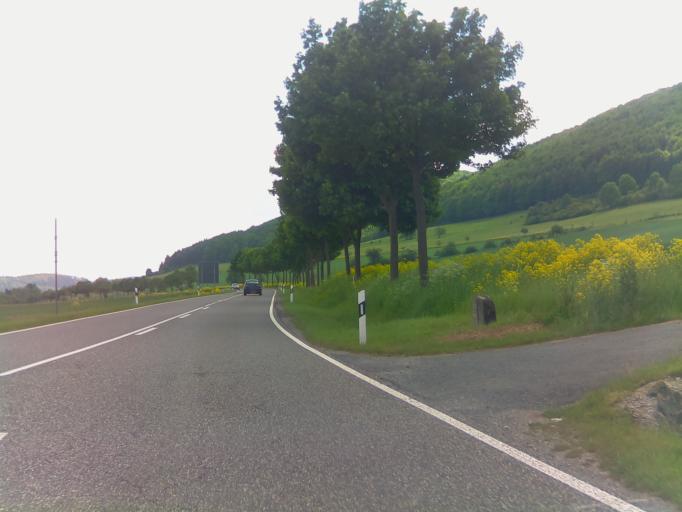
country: DE
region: Thuringia
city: Einhausen
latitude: 50.5235
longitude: 10.4740
